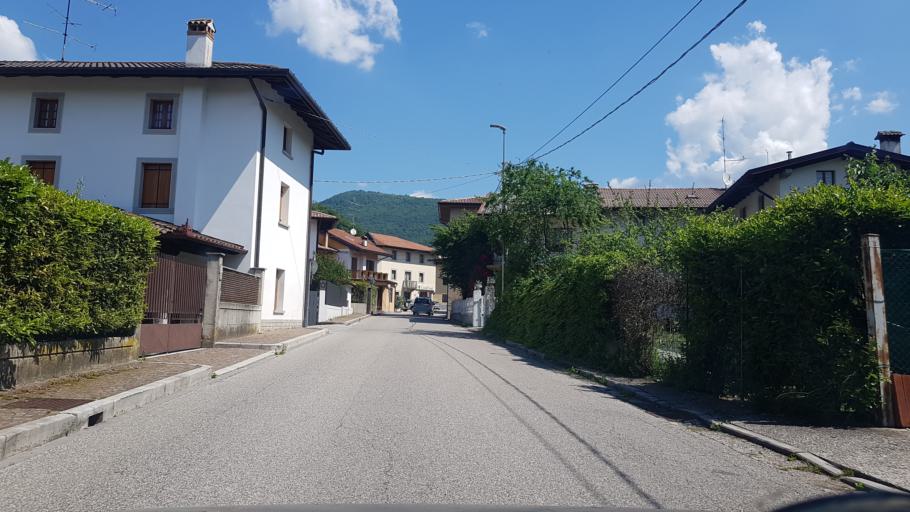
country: IT
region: Friuli Venezia Giulia
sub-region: Provincia di Udine
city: Torreano
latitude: 46.1302
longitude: 13.4327
